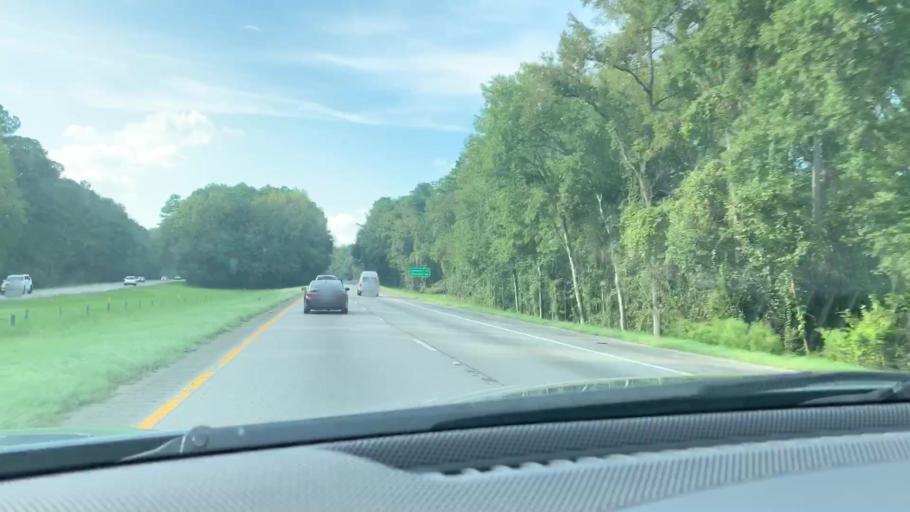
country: US
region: South Carolina
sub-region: Orangeburg County
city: Brookdale
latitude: 33.4656
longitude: -80.7394
